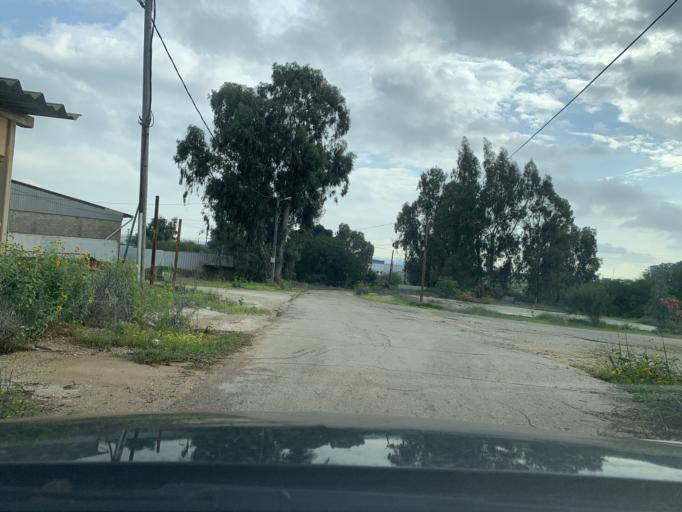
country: PS
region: West Bank
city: Qalqilyah
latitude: 32.1949
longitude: 34.9507
